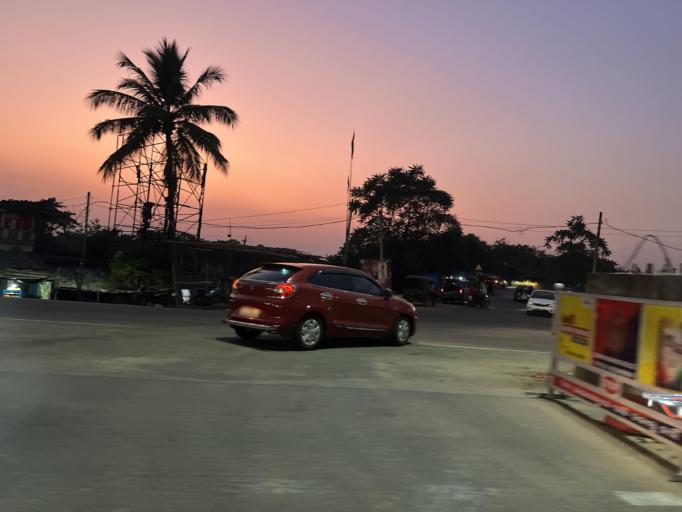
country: IN
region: Odisha
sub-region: Cuttack
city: Cuttack
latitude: 20.4283
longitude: 85.8775
